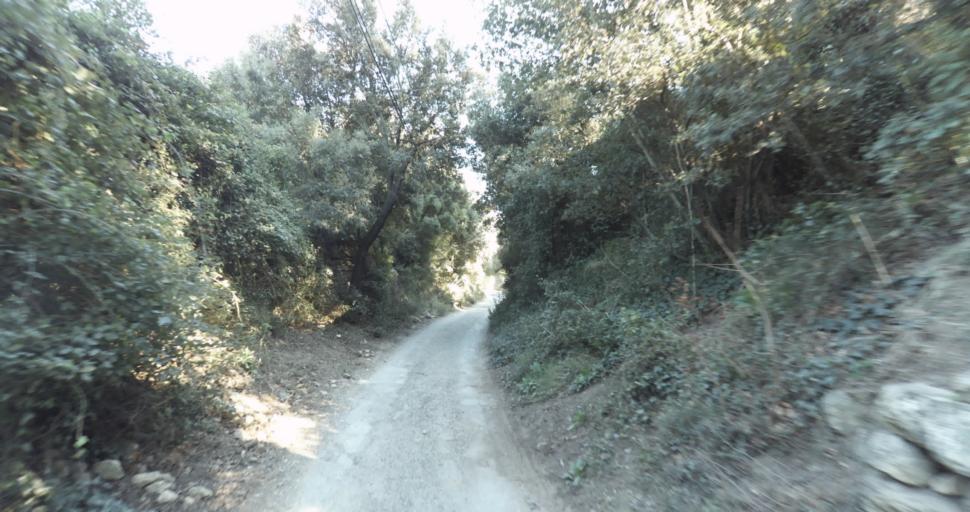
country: FR
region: Provence-Alpes-Cote d'Azur
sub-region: Departement des Bouches-du-Rhone
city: Pelissanne
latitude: 43.6453
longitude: 5.1435
